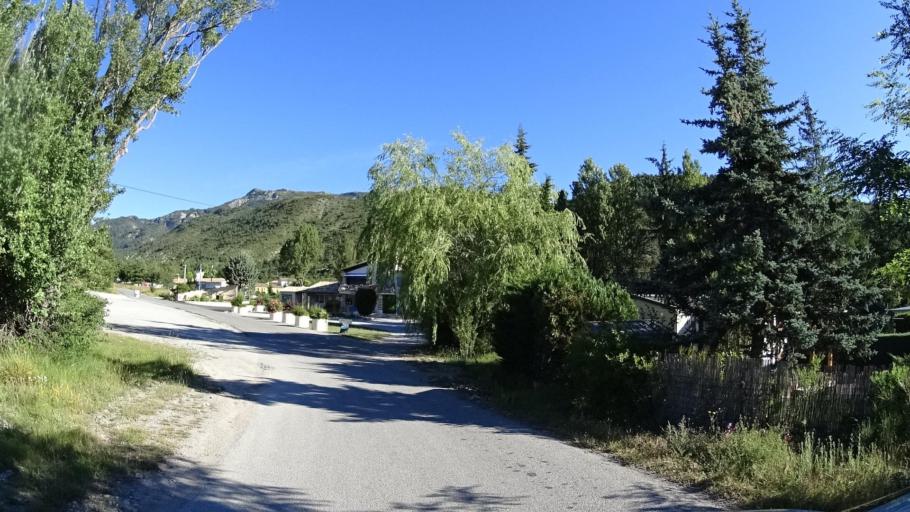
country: FR
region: Provence-Alpes-Cote d'Azur
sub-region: Departement des Alpes-de-Haute-Provence
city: Castellane
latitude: 43.8758
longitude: 6.5085
